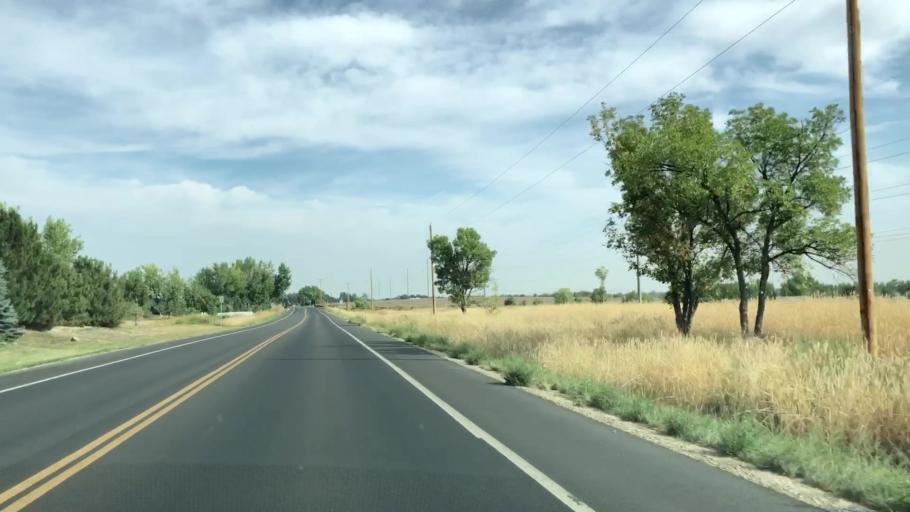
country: US
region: Colorado
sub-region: Larimer County
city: Loveland
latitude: 40.4359
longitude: -105.0454
